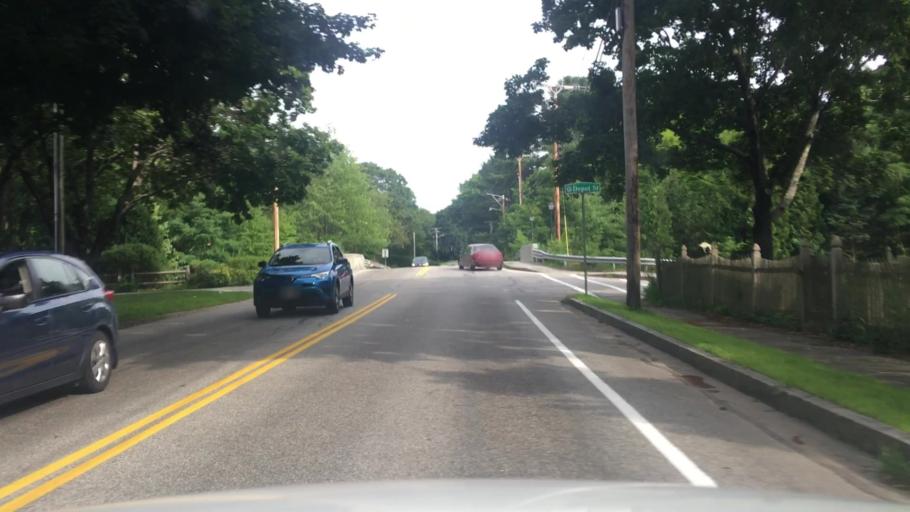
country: US
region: Maine
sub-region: York County
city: Kennebunk
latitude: 43.3838
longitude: -70.5289
